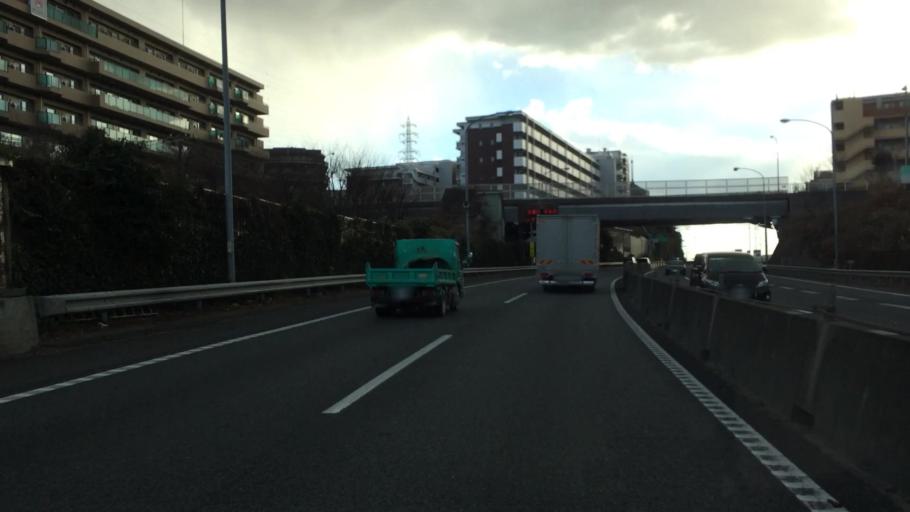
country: JP
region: Kanagawa
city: Yokohama
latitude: 35.4348
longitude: 139.5545
